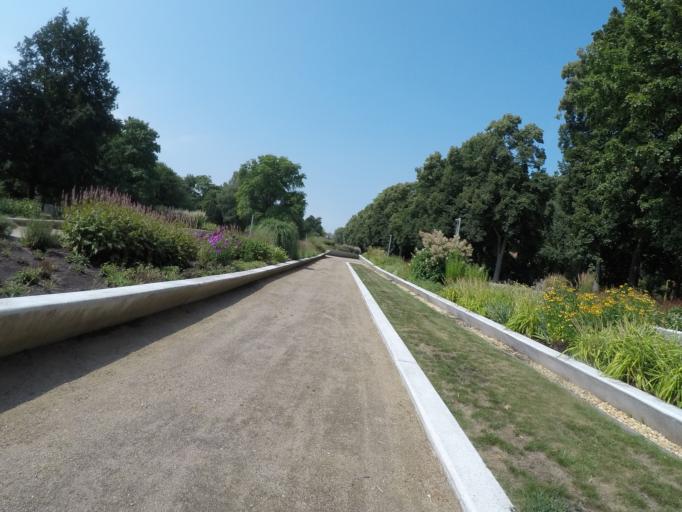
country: DE
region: Hamburg
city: Kleiner Grasbrook
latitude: 53.4993
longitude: 9.9945
